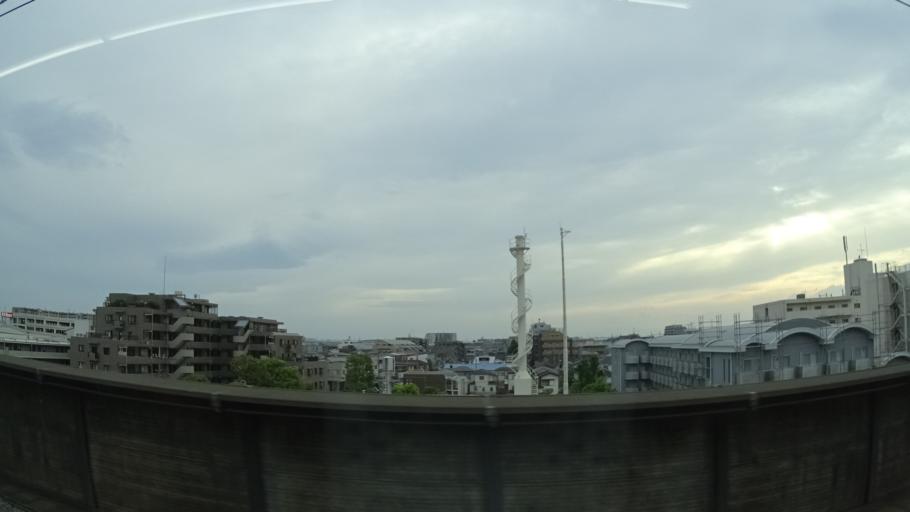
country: JP
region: Saitama
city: Shimotoda
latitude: 35.8366
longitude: 139.6516
